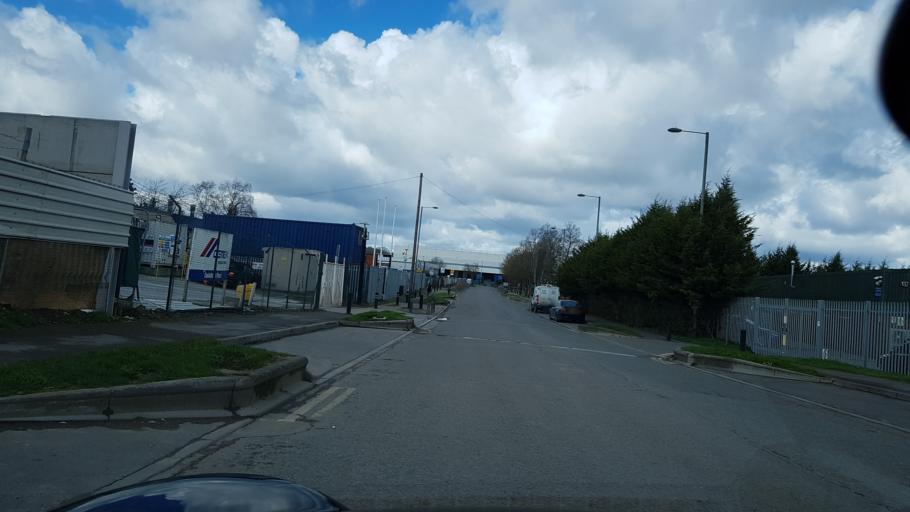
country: GB
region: England
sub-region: Surrey
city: Guildford
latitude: 51.2621
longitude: -0.5634
